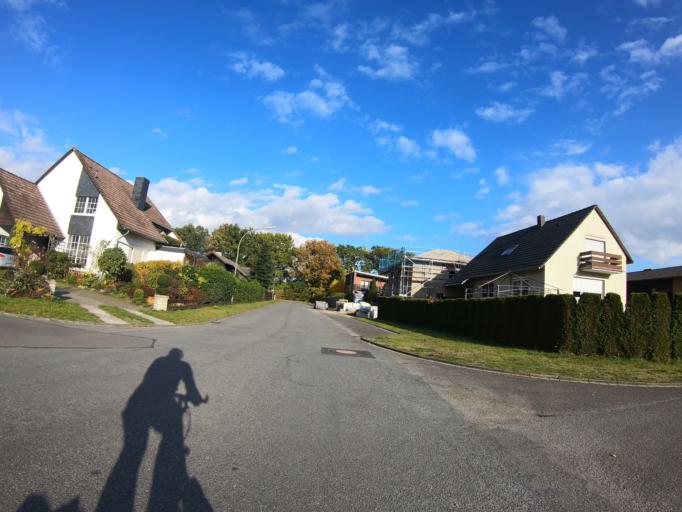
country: DE
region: Lower Saxony
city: Wagenhoff
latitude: 52.5154
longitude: 10.5449
